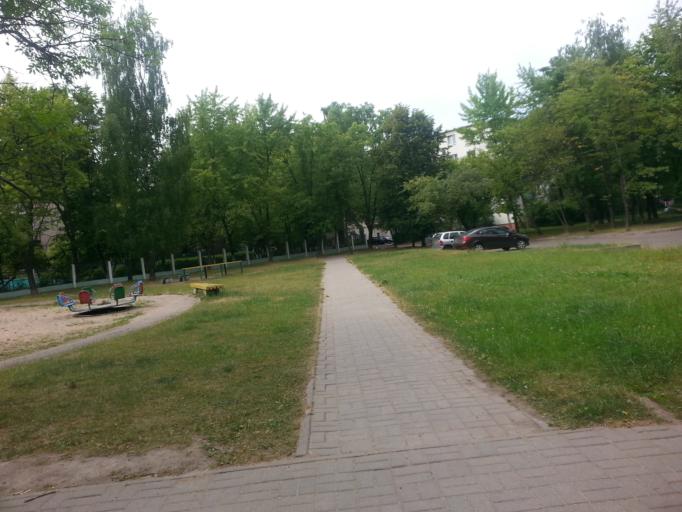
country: BY
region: Minsk
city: Novoye Medvezhino
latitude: 53.9130
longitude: 27.4936
